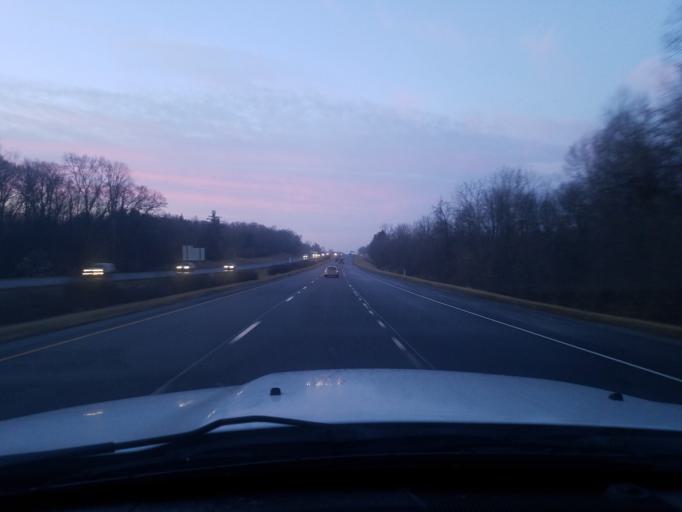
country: US
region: Indiana
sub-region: Huntington County
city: Roanoke
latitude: 40.9879
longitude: -85.2711
